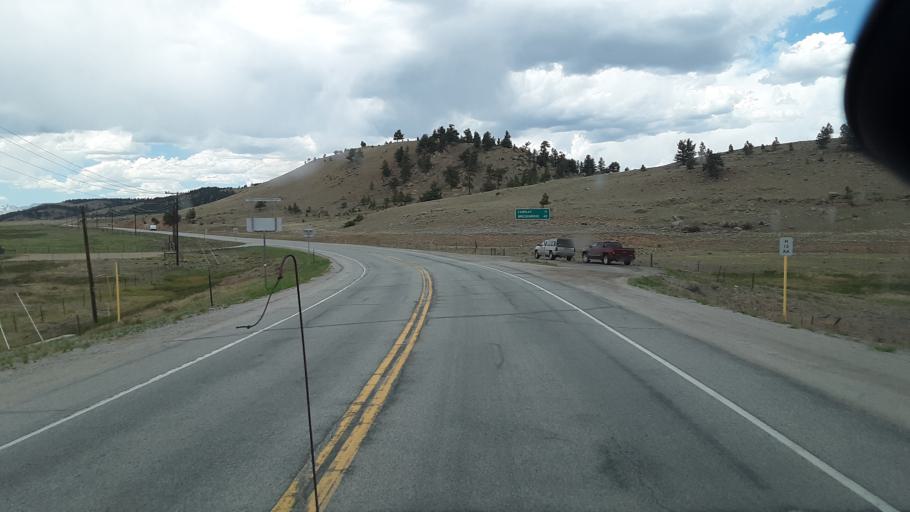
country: US
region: Colorado
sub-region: Park County
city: Fairplay
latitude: 39.0241
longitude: -105.8141
